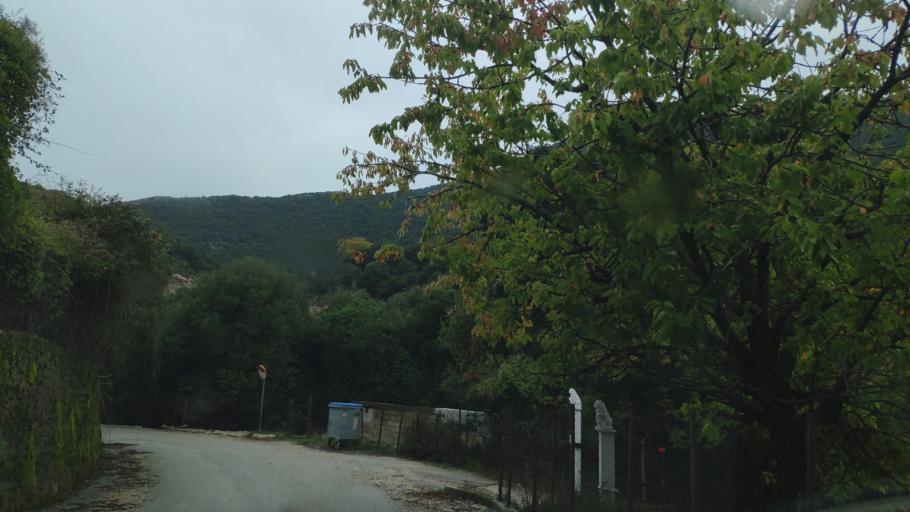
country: GR
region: Epirus
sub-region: Nomos Thesprotias
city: Paramythia
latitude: 39.4322
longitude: 20.6261
